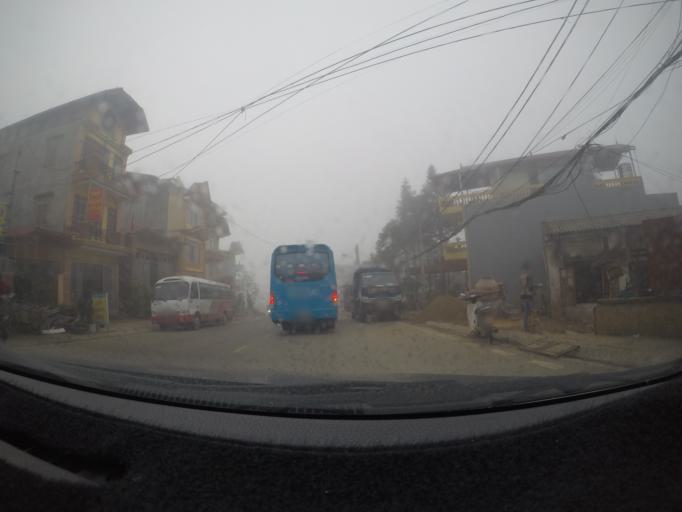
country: VN
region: Lao Cai
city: Sa Pa
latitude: 22.3400
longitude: 103.8426
